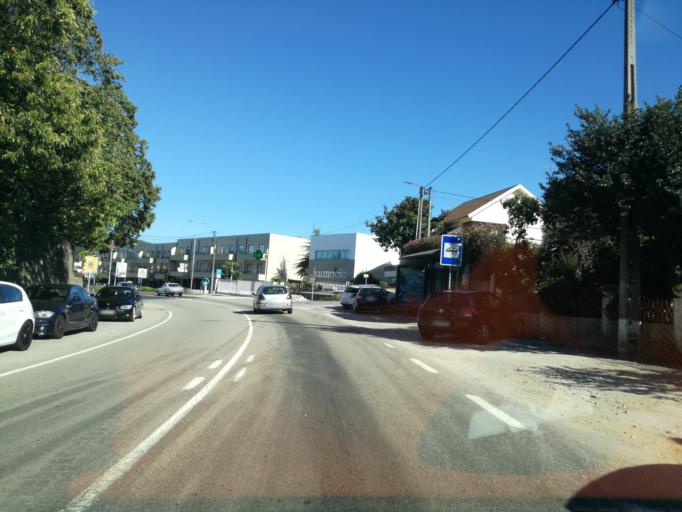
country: PT
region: Porto
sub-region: Valongo
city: Alfena
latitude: 41.2592
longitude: -8.4868
